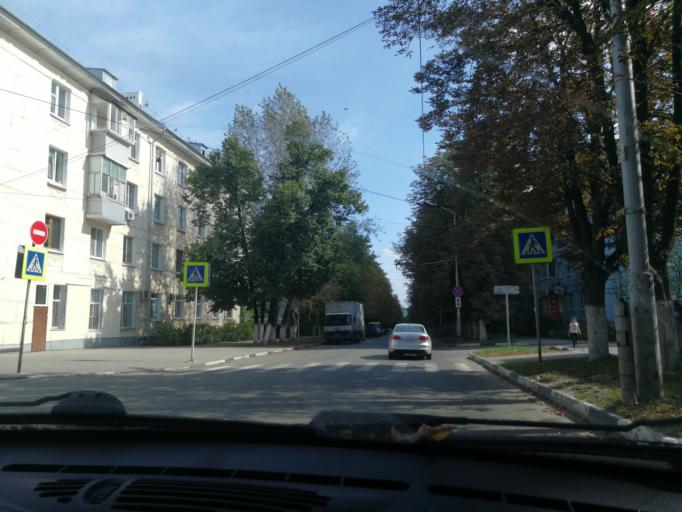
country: RU
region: Rjazan
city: Ryazan'
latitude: 54.6091
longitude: 39.7184
